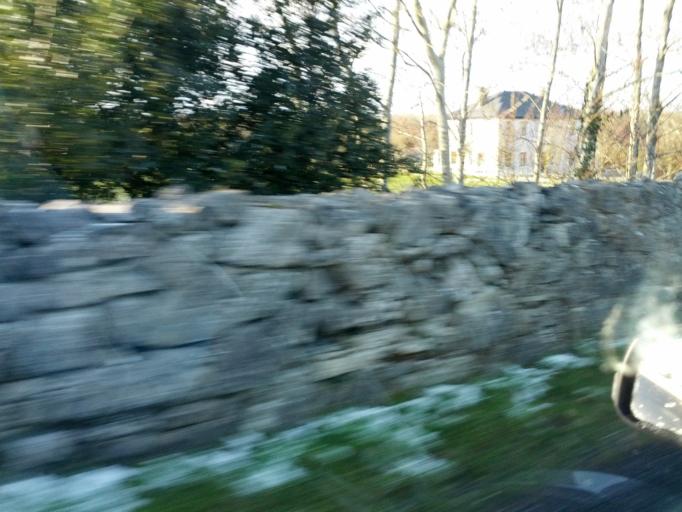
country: IE
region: Connaught
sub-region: County Galway
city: Gort
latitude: 53.1497
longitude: -8.7923
